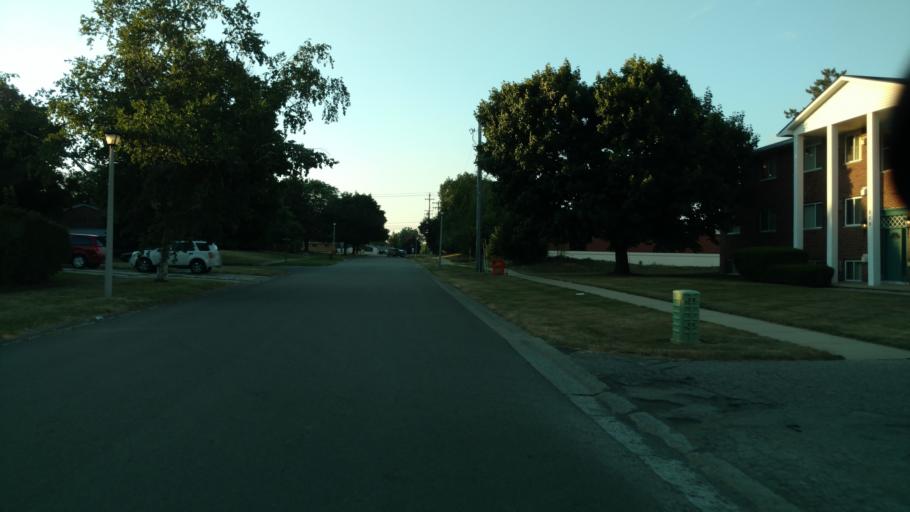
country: US
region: Michigan
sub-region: Eaton County
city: Waverly
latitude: 42.7249
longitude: -84.6072
